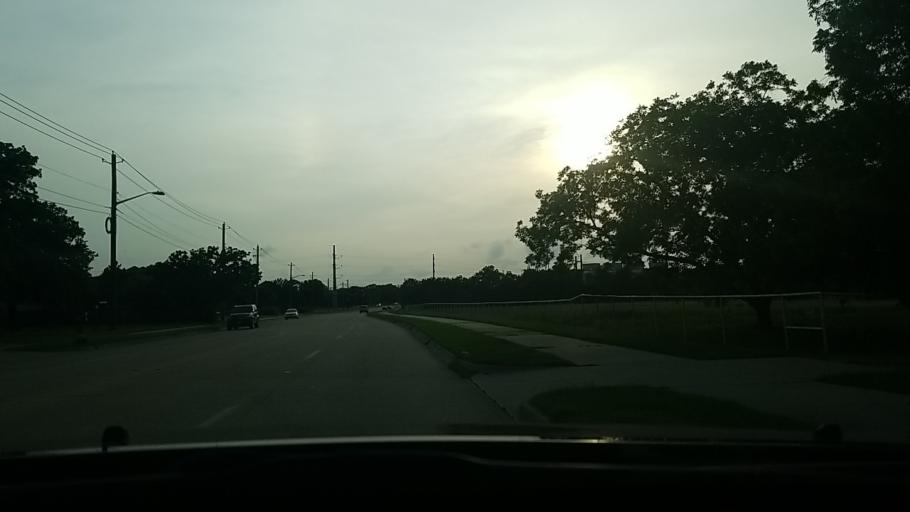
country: US
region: Texas
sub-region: Denton County
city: Denton
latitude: 33.1960
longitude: -97.1011
